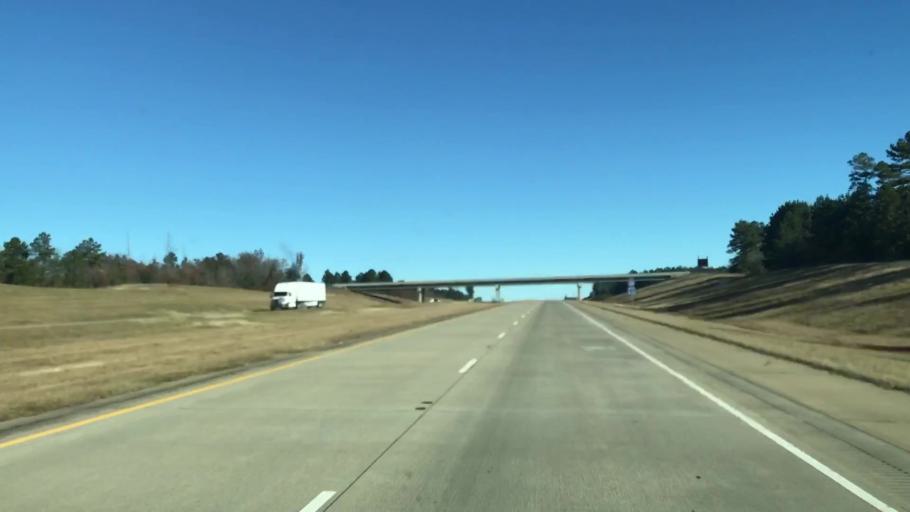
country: US
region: Louisiana
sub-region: Caddo Parish
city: Vivian
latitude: 33.0052
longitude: -93.9061
